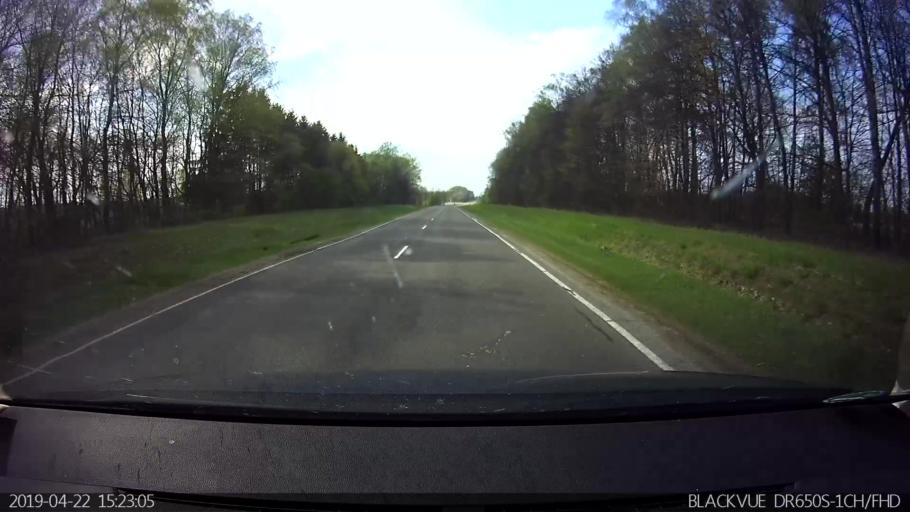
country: BY
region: Brest
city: Vysokaye
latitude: 52.3531
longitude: 23.4334
